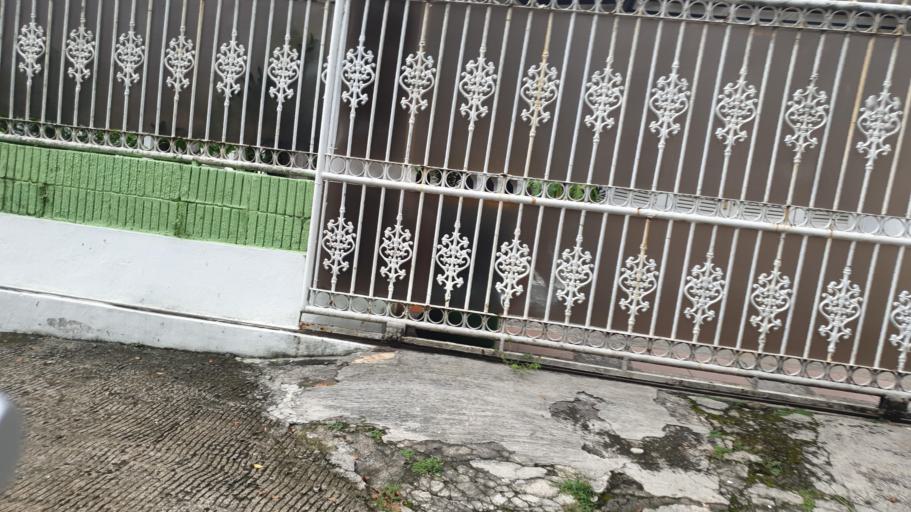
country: ID
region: West Java
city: Pamulang
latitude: -6.3039
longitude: 106.7899
